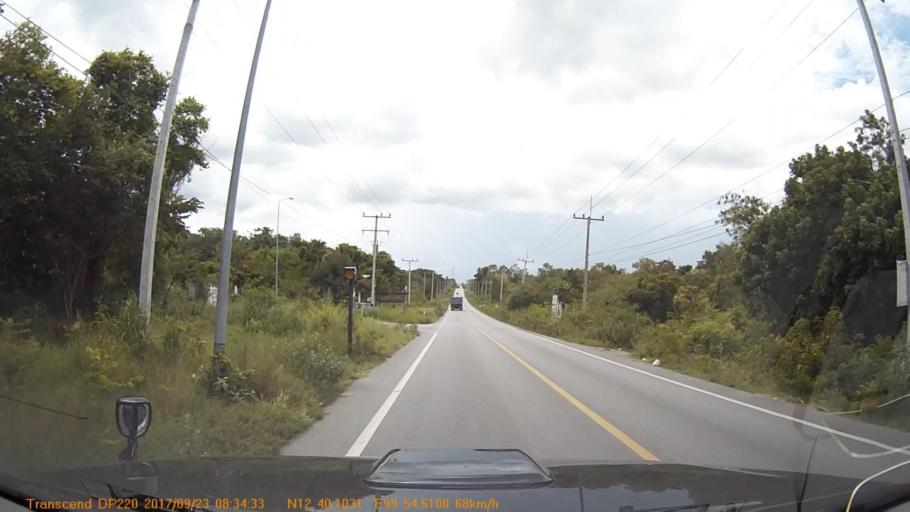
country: TH
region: Prachuap Khiri Khan
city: Hua Hin
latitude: 12.6684
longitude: 99.9086
